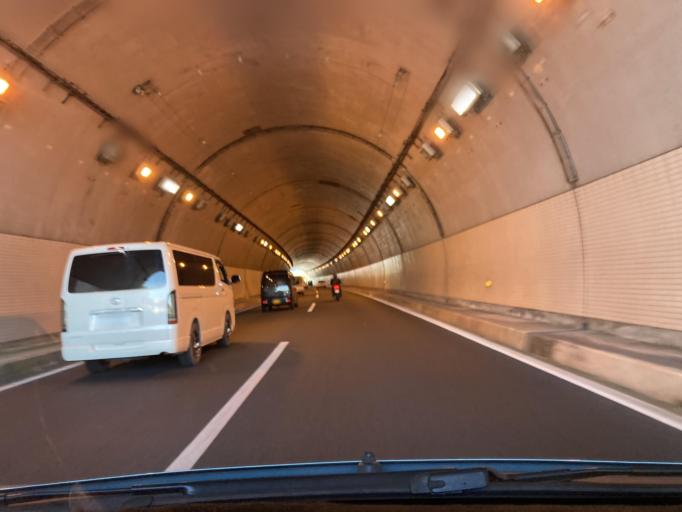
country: JP
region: Okinawa
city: Chatan
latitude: 26.3087
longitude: 127.7884
